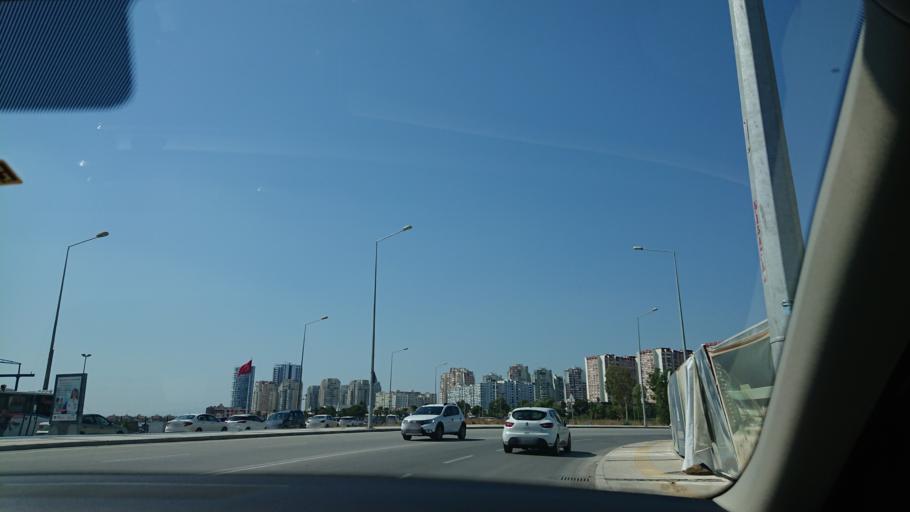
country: TR
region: Izmir
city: Karsiyaka
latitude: 38.4665
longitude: 27.0809
